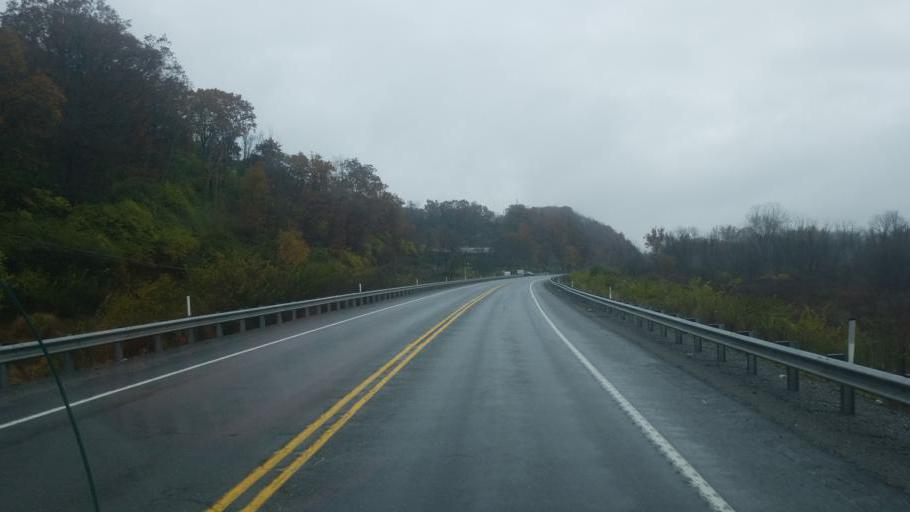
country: US
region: Pennsylvania
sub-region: Centre County
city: Milesburg
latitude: 40.9742
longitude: -77.7477
